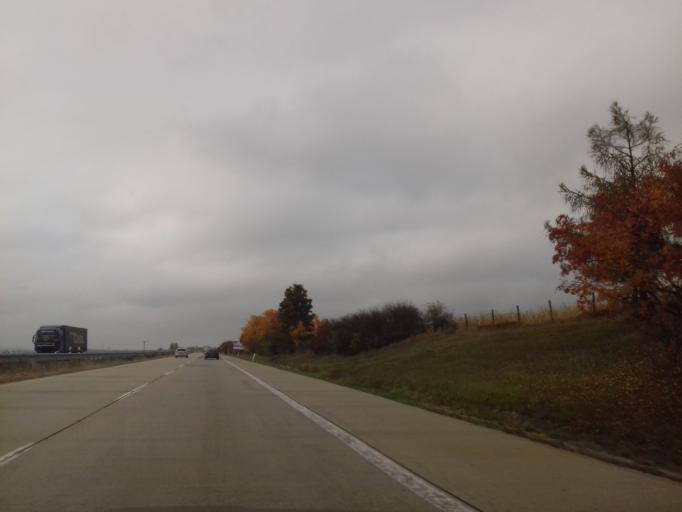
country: CZ
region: South Moravian
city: Velke Pavlovice
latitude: 48.8930
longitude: 16.8014
